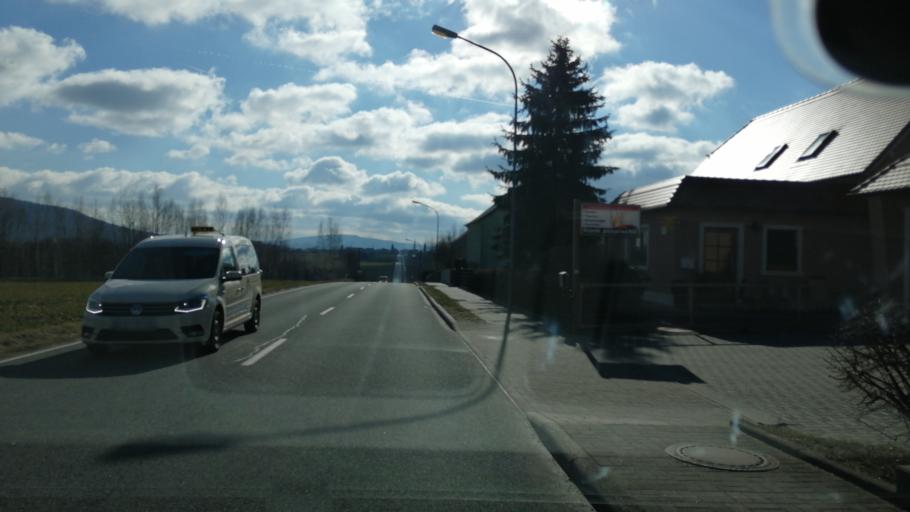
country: DE
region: Saxony
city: Lobau
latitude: 51.1216
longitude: 14.6747
